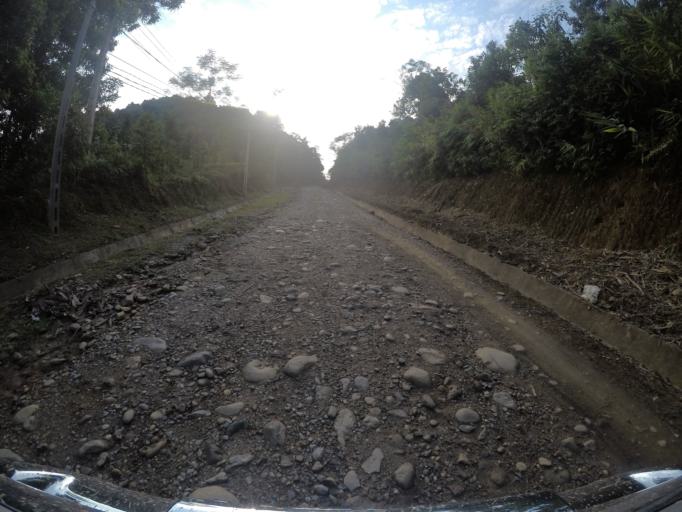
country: VN
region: Yen Bai
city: Son Thinh
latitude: 21.6828
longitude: 104.6232
